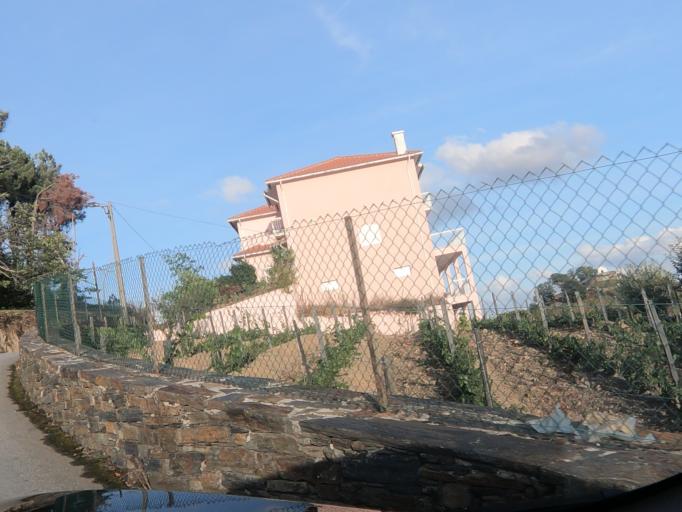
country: PT
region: Vila Real
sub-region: Santa Marta de Penaguiao
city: Santa Marta de Penaguiao
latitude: 41.2291
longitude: -7.8079
